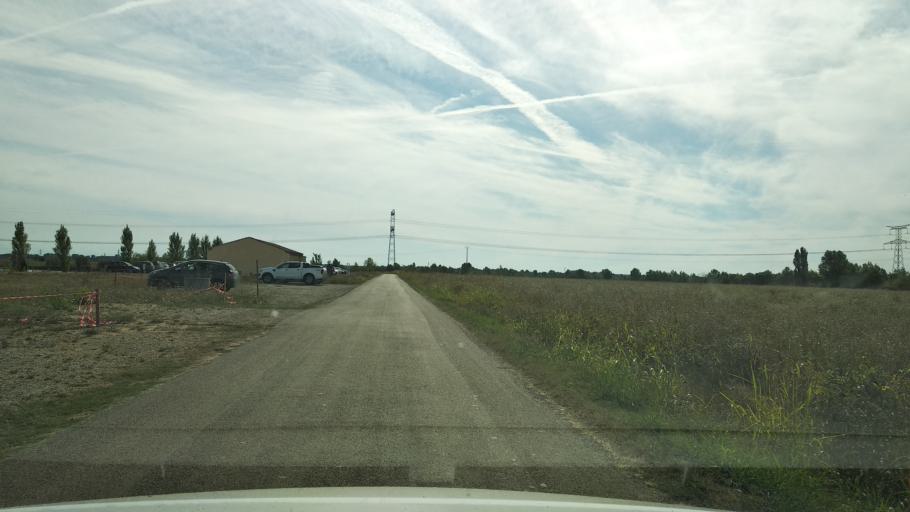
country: FR
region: Midi-Pyrenees
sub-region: Departement du Tarn-et-Garonne
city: Pompignan
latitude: 43.8057
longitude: 1.3101
